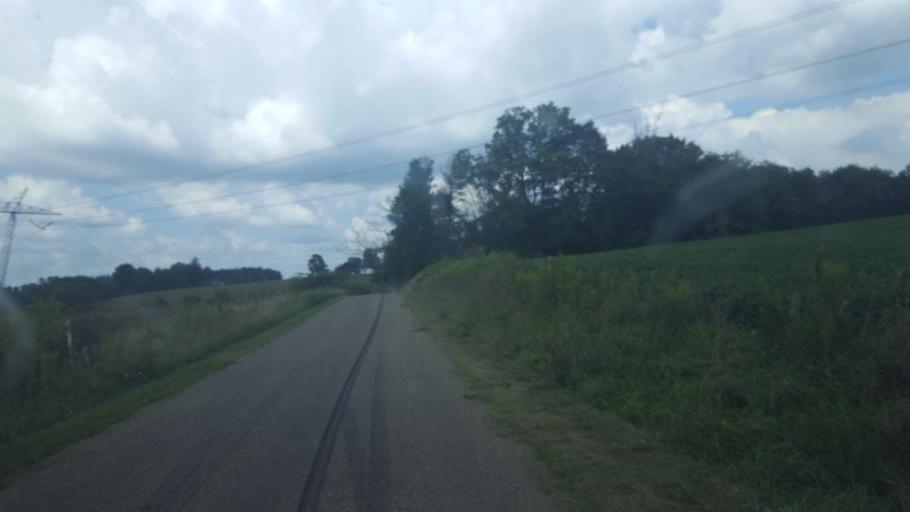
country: US
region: Ohio
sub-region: Knox County
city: Gambier
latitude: 40.3620
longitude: -82.3246
